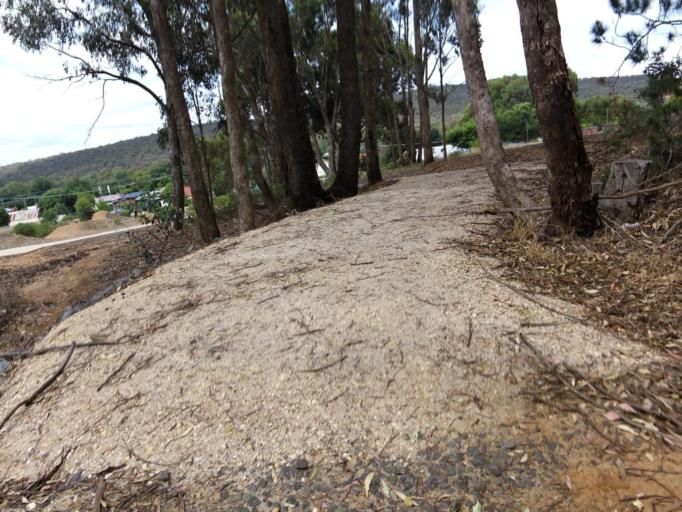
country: AU
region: Victoria
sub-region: Greater Bendigo
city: Kennington
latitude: -36.9254
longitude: 144.7083
